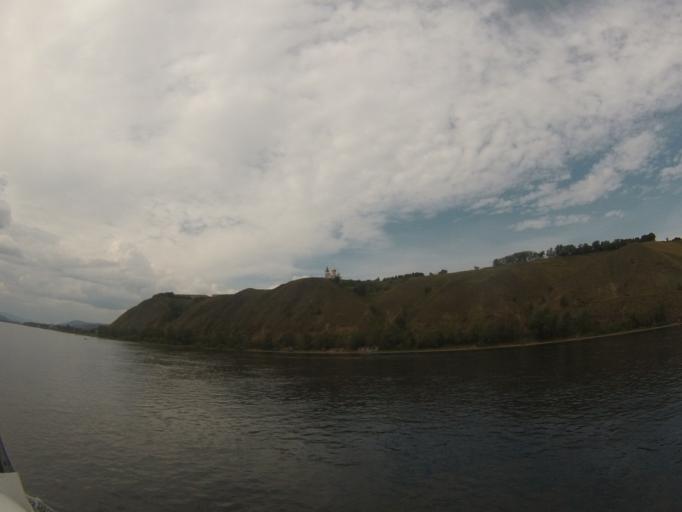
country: RU
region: Krasnoyarskiy
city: Krasnoyarsk
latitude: 55.9814
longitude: 92.7744
